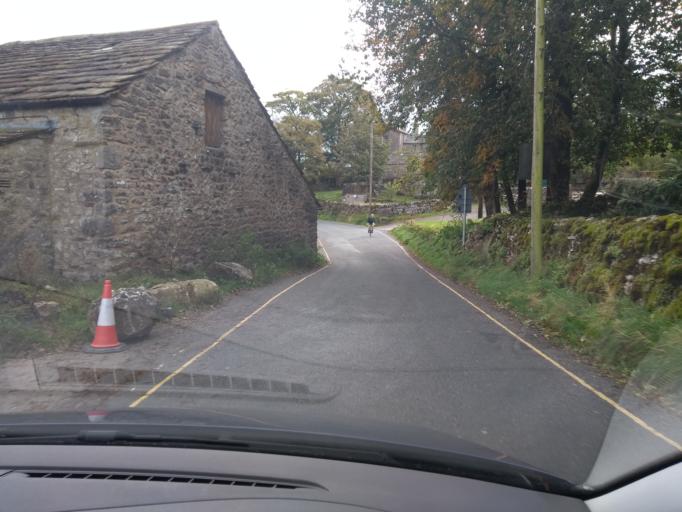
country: GB
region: England
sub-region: North Yorkshire
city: Gargrave
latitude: 54.0650
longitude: -2.1561
